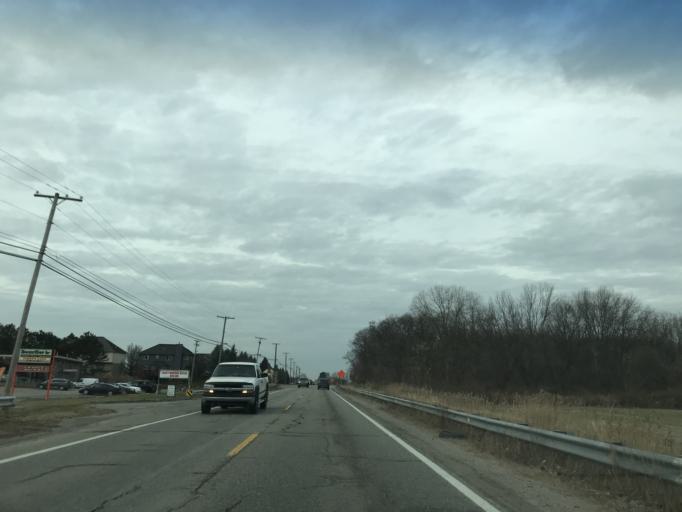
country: US
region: Michigan
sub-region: Macomb County
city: Mount Clemens
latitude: 42.6733
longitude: -82.8893
